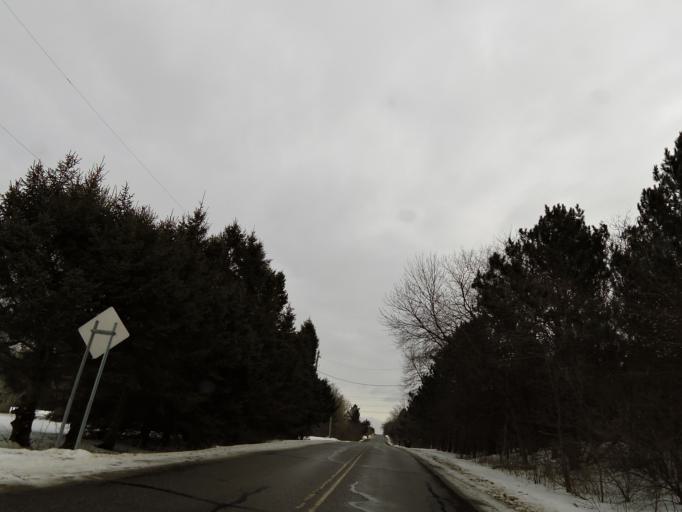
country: US
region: Minnesota
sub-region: Washington County
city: Oak Park Heights
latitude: 44.9926
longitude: -92.8205
